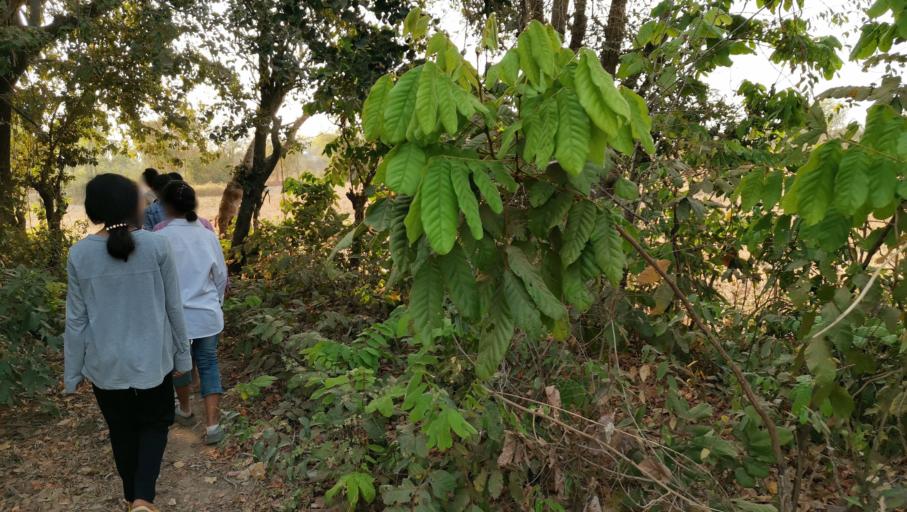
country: KH
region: Battambang
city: Battambang
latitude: 13.0452
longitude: 103.1616
